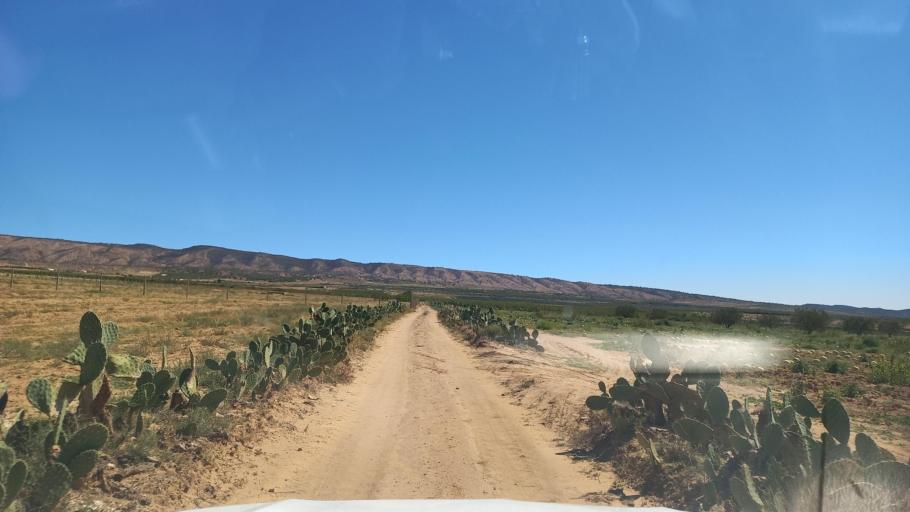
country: TN
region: Al Qasrayn
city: Sbiba
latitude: 35.3488
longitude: 9.1025
